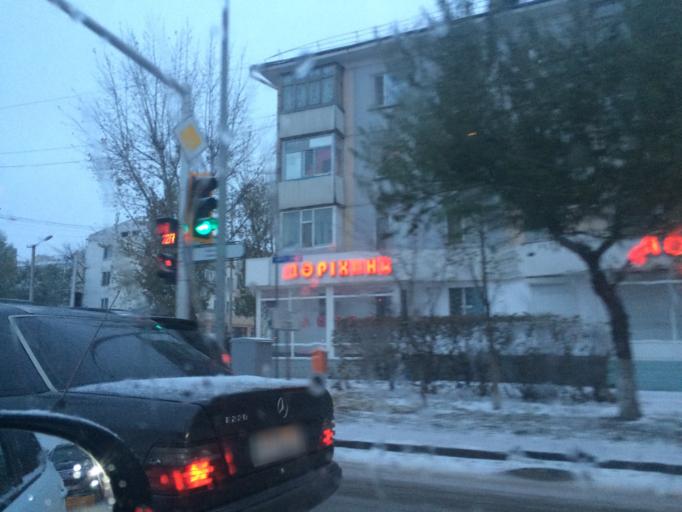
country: KZ
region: Astana Qalasy
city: Astana
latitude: 51.1819
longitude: 71.4092
